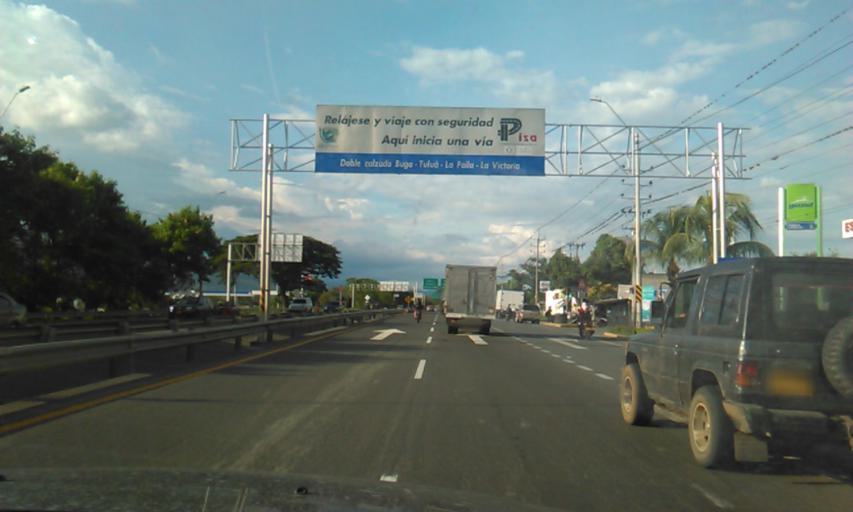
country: CO
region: Valle del Cauca
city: Buga
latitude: 3.8947
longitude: -76.3122
